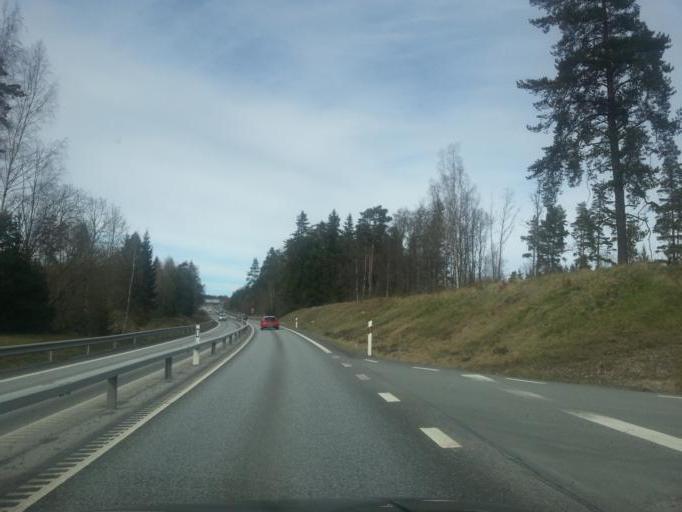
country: SE
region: Joenkoeping
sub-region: Jonkopings Kommun
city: Bankeryd
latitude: 57.8780
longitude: 14.1044
